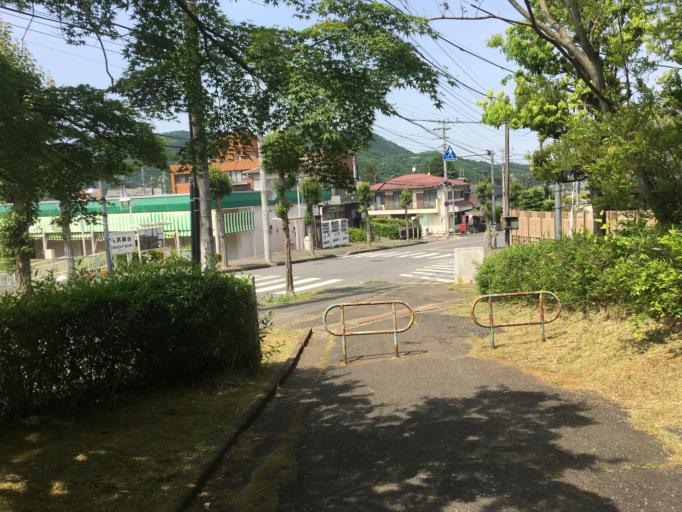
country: JP
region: Saitama
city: Hanno
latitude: 35.8794
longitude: 139.3026
